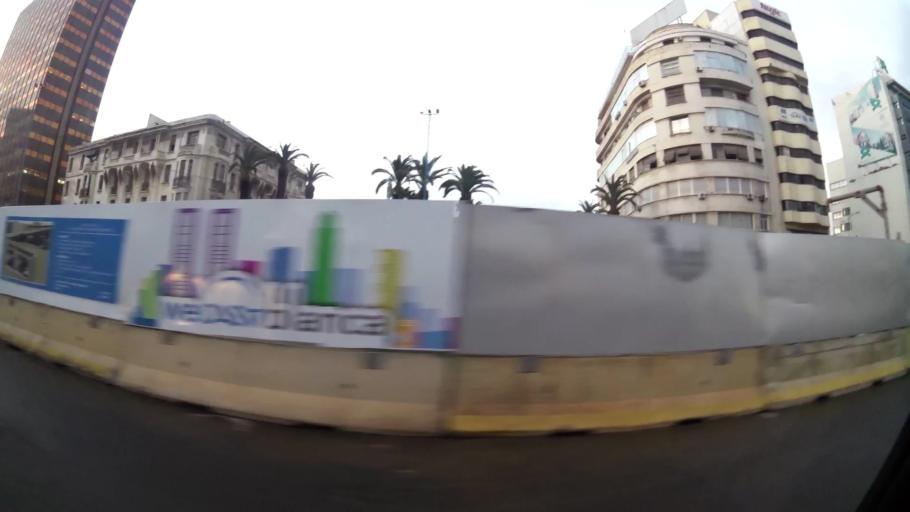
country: MA
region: Grand Casablanca
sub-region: Casablanca
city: Casablanca
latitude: 33.5967
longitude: -7.6095
